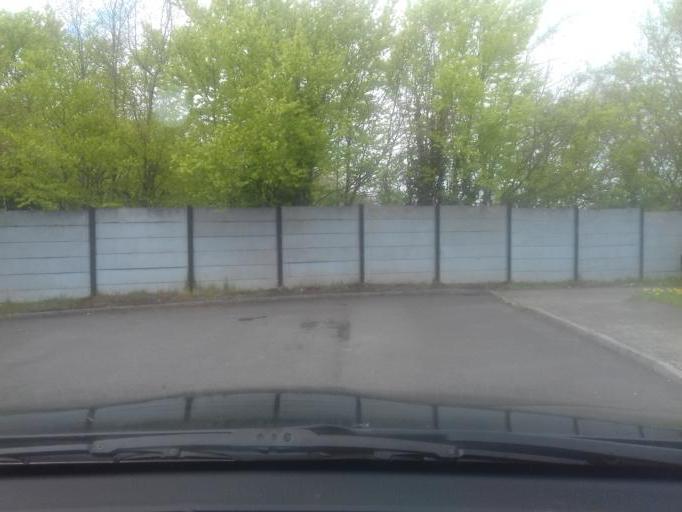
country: IE
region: Leinster
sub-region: Laois
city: Portlaoise
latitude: 53.0457
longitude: -7.3100
